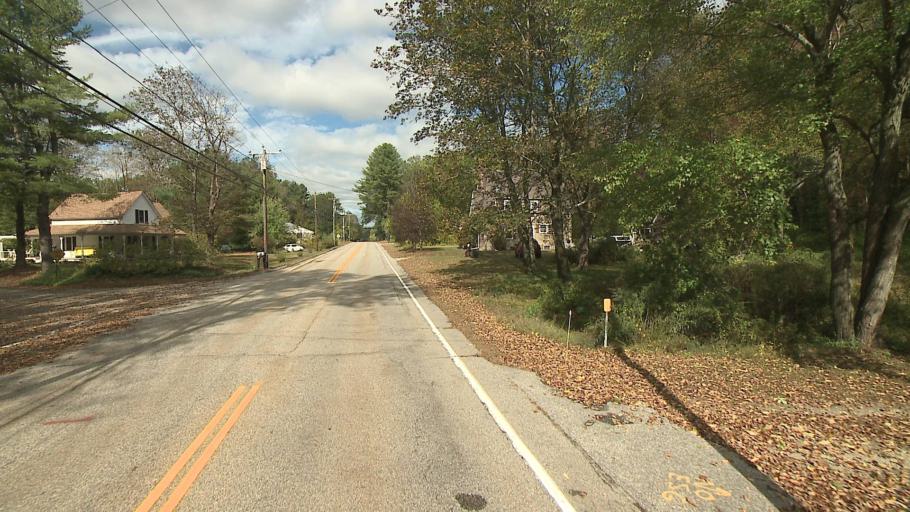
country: US
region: Connecticut
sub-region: Windham County
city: Putnam
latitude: 41.9024
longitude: -71.8902
